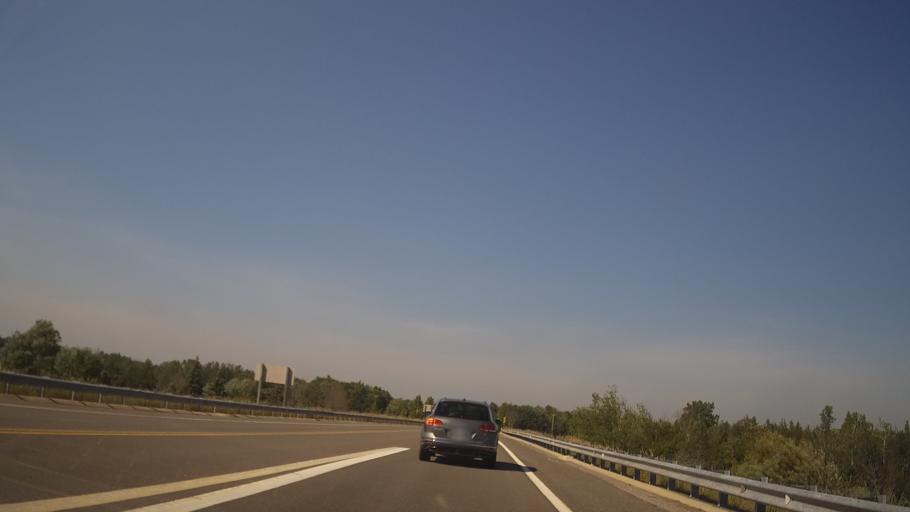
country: US
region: Michigan
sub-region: Ogemaw County
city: Skidway Lake
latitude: 44.1340
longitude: -84.1295
